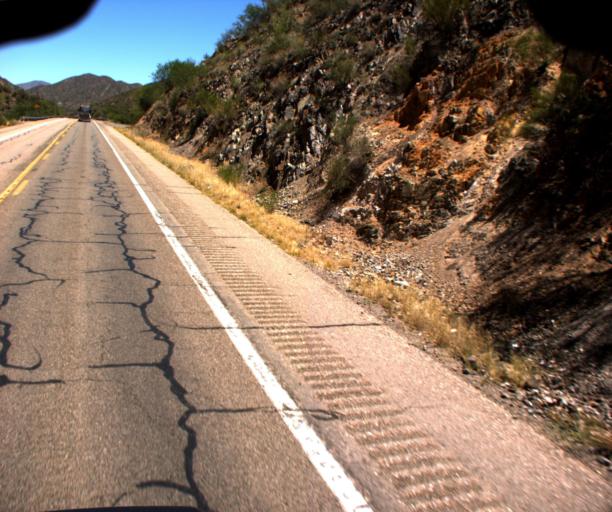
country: US
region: Arizona
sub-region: Pinal County
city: Kearny
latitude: 33.0120
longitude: -110.7503
